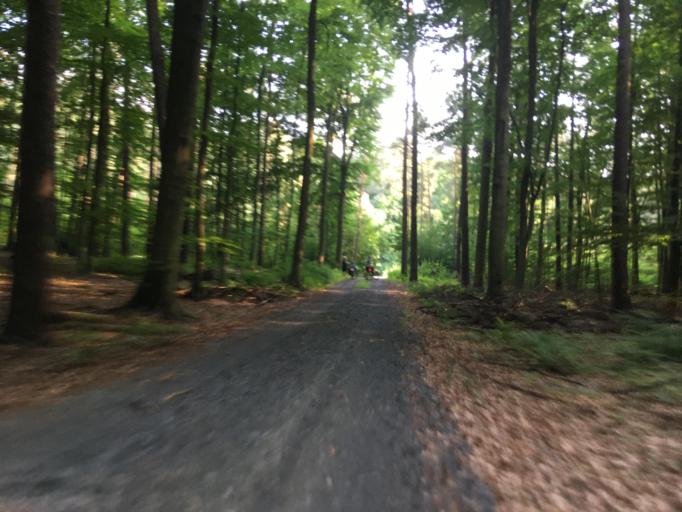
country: DE
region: Brandenburg
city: Wandlitz
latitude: 52.7305
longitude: 13.5297
